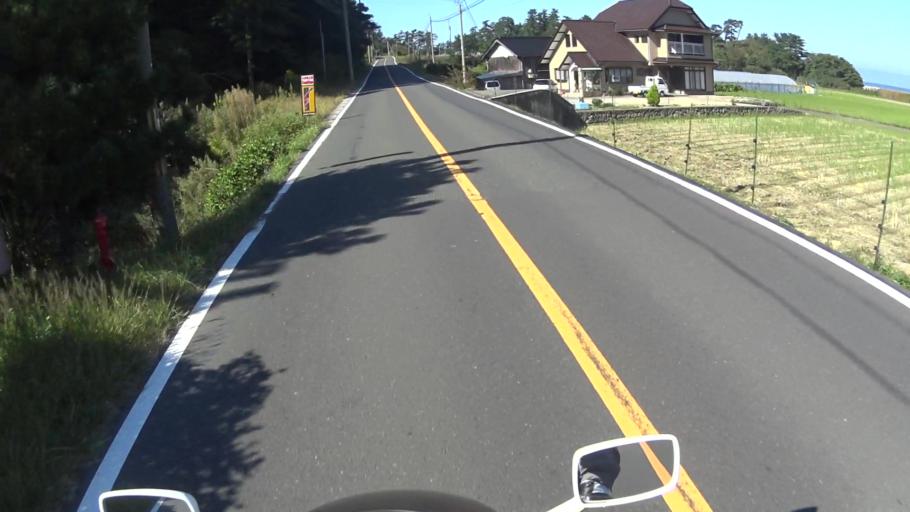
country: JP
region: Kyoto
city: Miyazu
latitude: 35.7470
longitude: 135.1620
